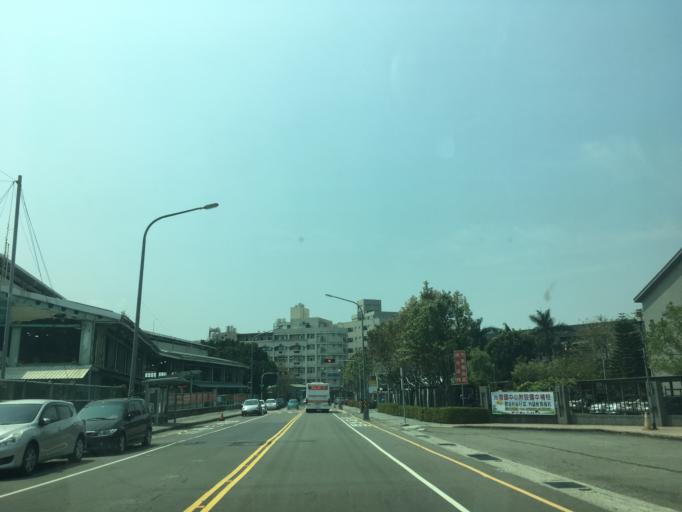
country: TW
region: Taiwan
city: Zhongxing New Village
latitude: 24.0431
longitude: 120.6904
